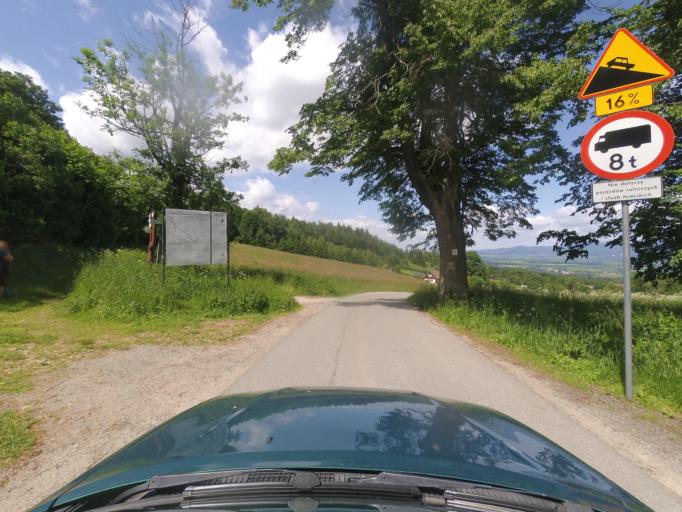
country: PL
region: Lower Silesian Voivodeship
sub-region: Powiat klodzki
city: Miedzylesie
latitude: 50.1157
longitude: 16.6299
